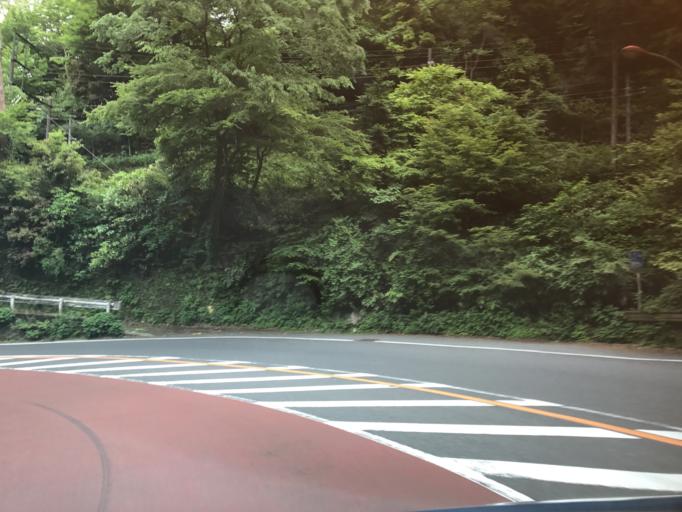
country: JP
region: Kanagawa
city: Hakone
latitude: 35.2386
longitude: 139.0671
